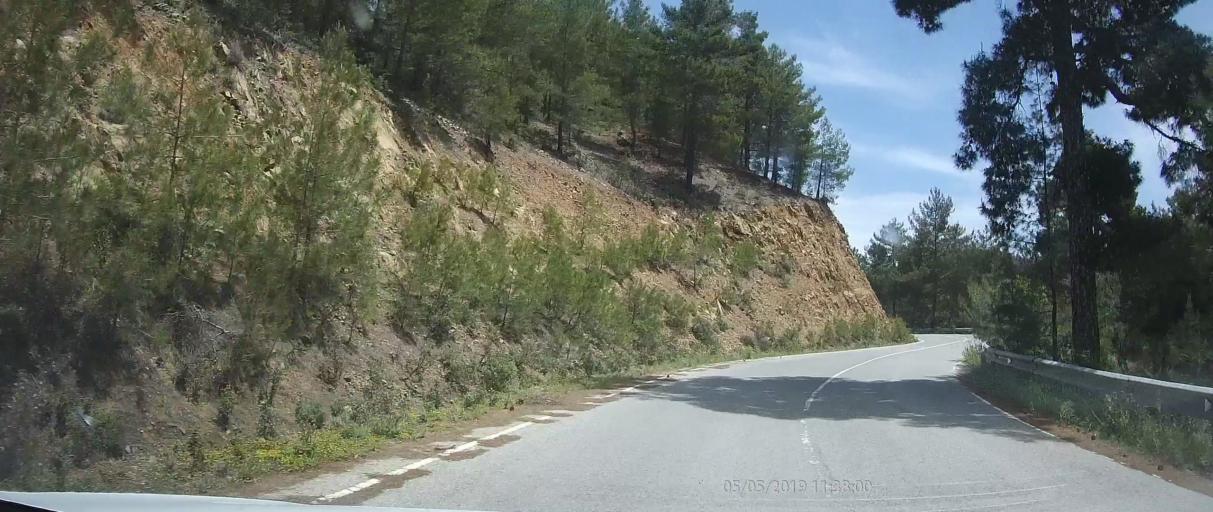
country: CY
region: Lefkosia
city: Kato Pyrgos
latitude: 34.9765
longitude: 32.6602
